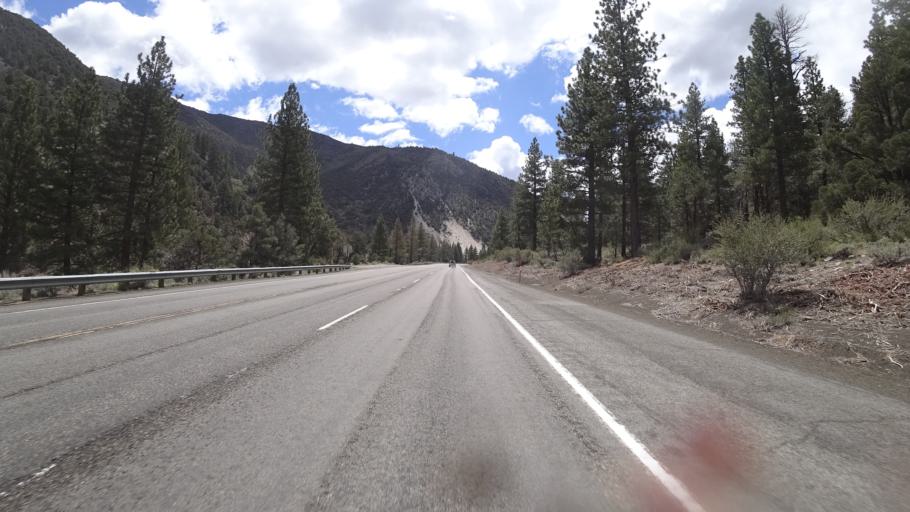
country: US
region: California
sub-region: Mono County
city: Bridgeport
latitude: 38.4240
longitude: -119.4493
